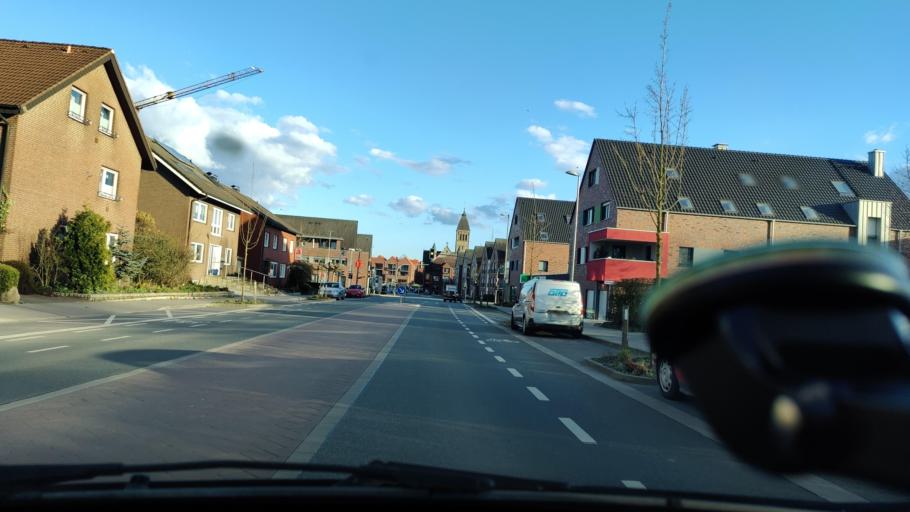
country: DE
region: North Rhine-Westphalia
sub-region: Regierungsbezirk Munster
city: Coesfeld
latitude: 51.8988
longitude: 7.1891
